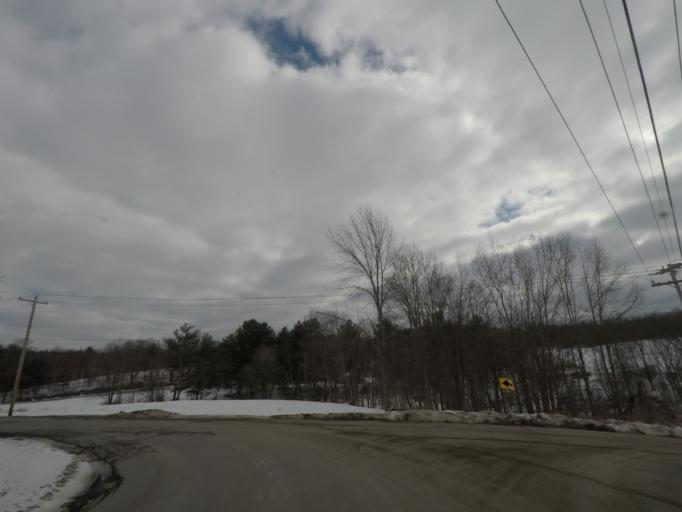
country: US
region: New York
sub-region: Rensselaer County
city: Hoosick Falls
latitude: 42.9188
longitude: -73.4321
